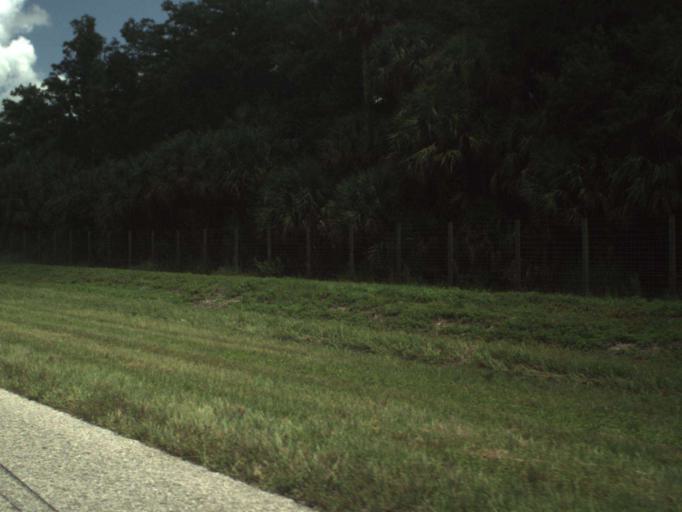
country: US
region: Florida
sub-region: Indian River County
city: Fellsmere
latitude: 27.6610
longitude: -80.7932
